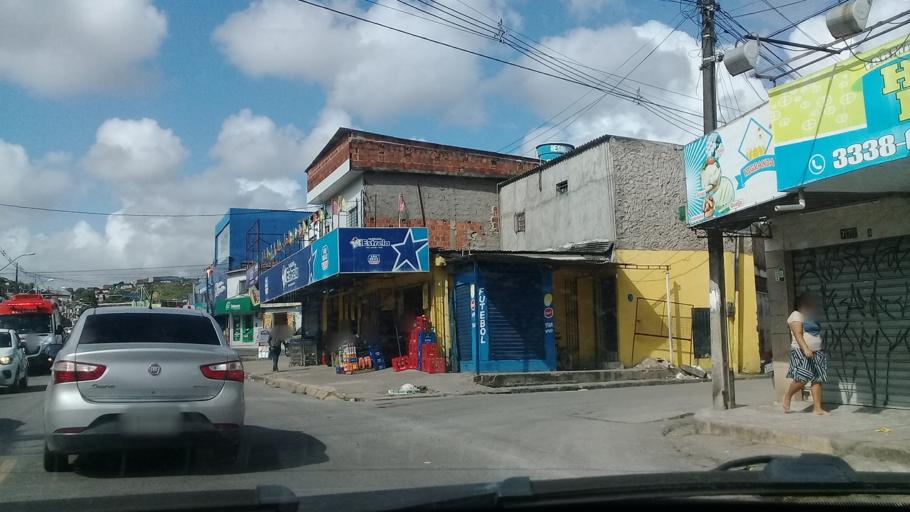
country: BR
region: Pernambuco
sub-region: Jaboatao Dos Guararapes
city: Jaboatao dos Guararapes
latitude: -8.1158
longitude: -34.9404
